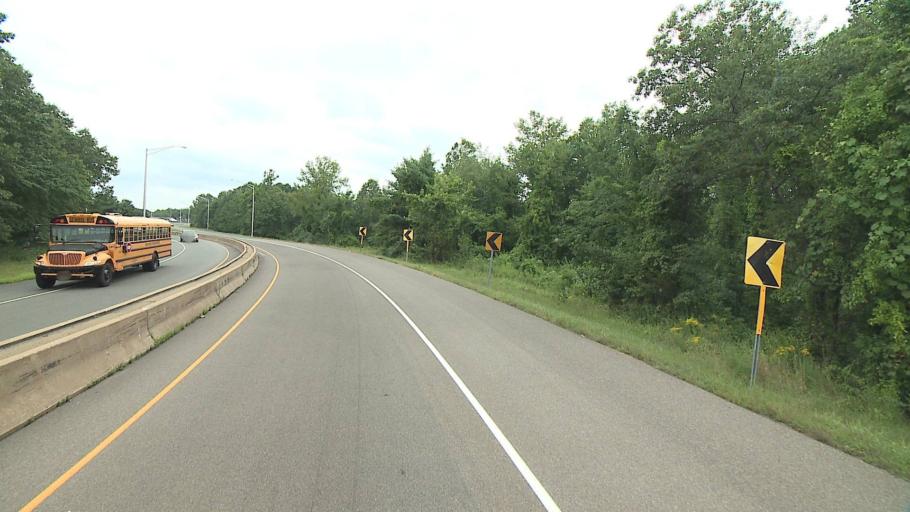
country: US
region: Connecticut
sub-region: Hartford County
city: Glastonbury
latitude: 41.7309
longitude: -72.6124
